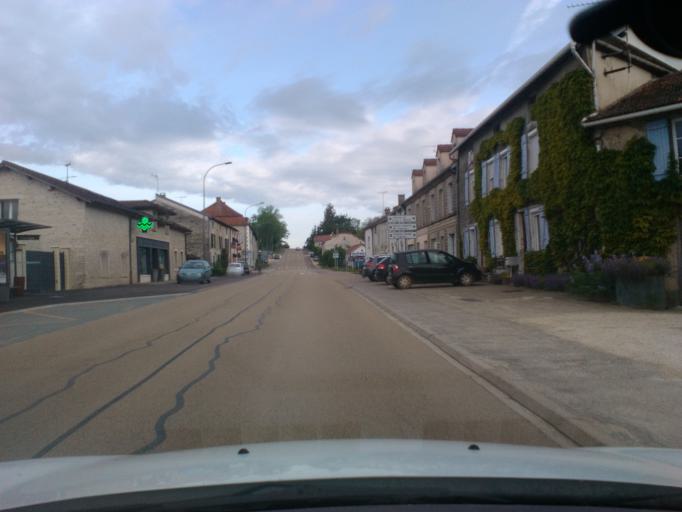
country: FR
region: Champagne-Ardenne
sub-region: Departement de la Haute-Marne
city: Lavilleneuve-au-Roi
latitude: 48.2250
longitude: 4.8892
